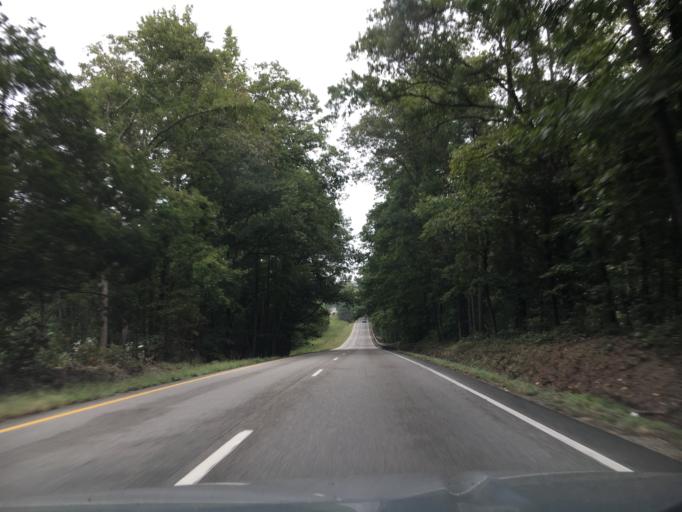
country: US
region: Virginia
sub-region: Chesterfield County
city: Woodlake
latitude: 37.5081
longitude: -77.7492
